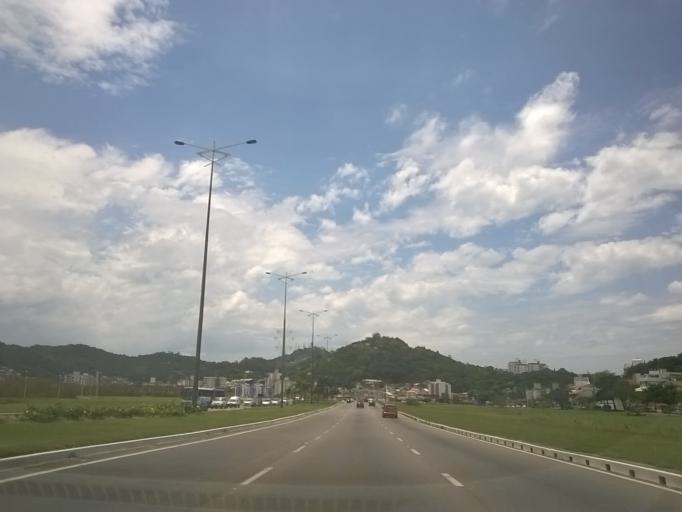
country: BR
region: Santa Catarina
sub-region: Florianopolis
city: Saco dos Limoes
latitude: -27.6190
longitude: -48.5281
